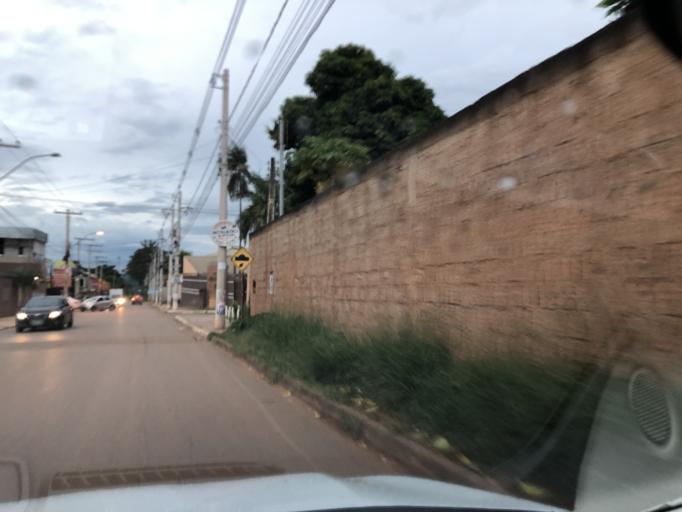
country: BR
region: Goias
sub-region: Luziania
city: Luziania
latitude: -16.1100
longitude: -47.9850
